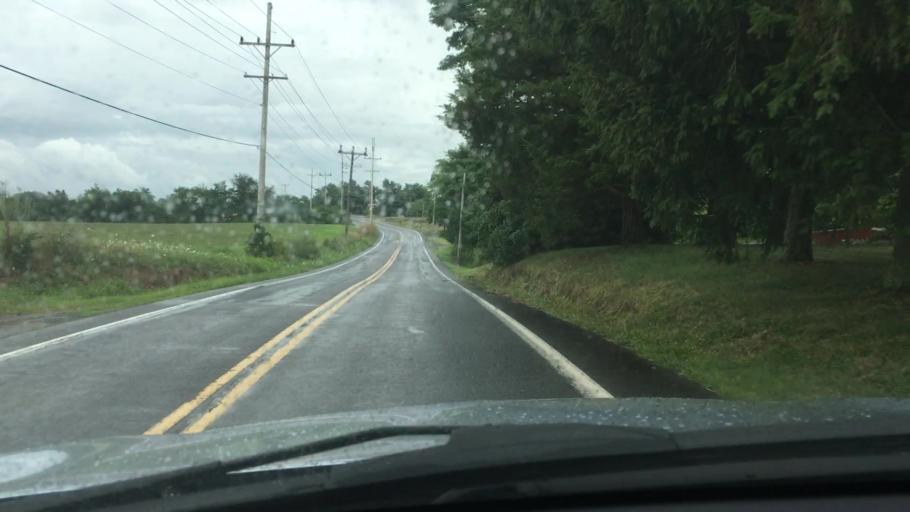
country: US
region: Pennsylvania
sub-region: Franklin County
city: Greencastle
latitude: 39.8625
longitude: -77.7526
